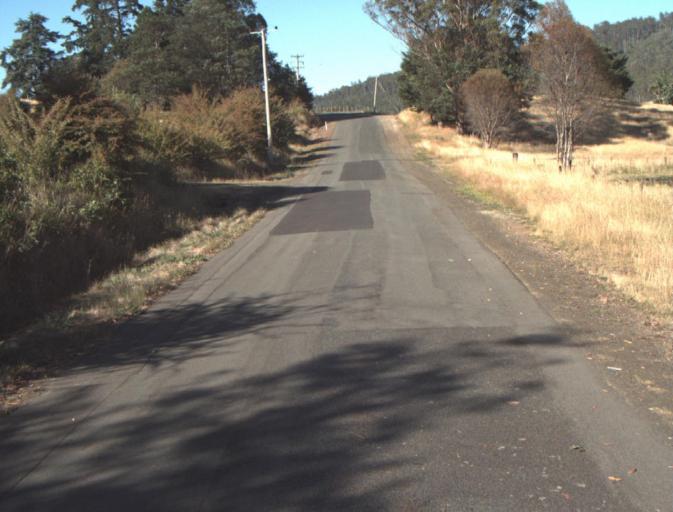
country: AU
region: Tasmania
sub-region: Launceston
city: Newstead
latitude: -41.3490
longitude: 147.3042
